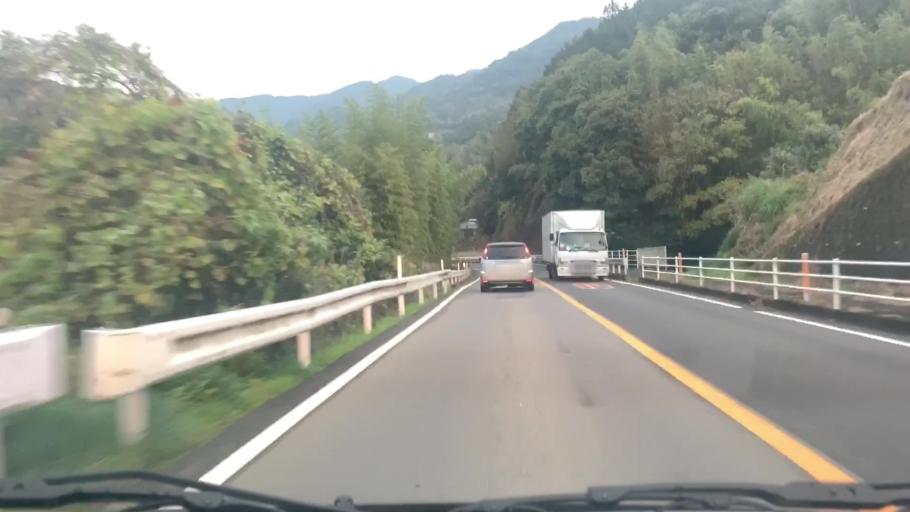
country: JP
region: Saga Prefecture
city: Ureshinomachi-shimojuku
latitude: 33.0535
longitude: 129.9373
